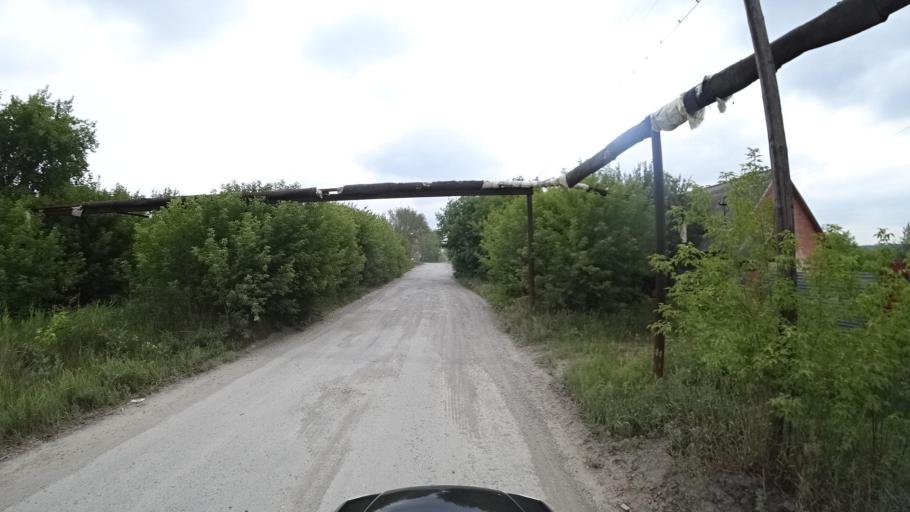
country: RU
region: Sverdlovsk
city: Kamyshlov
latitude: 56.8326
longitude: 62.7220
